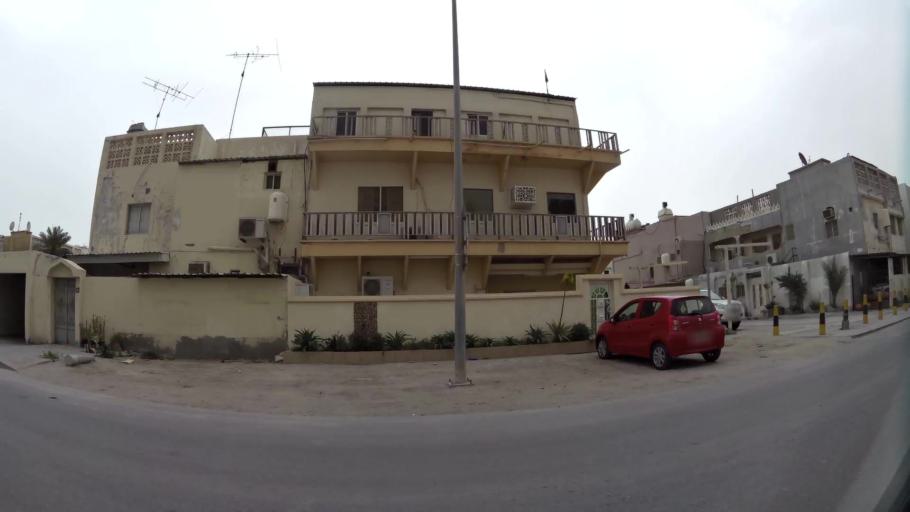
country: BH
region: Northern
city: Madinat `Isa
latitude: 26.1733
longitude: 50.5430
